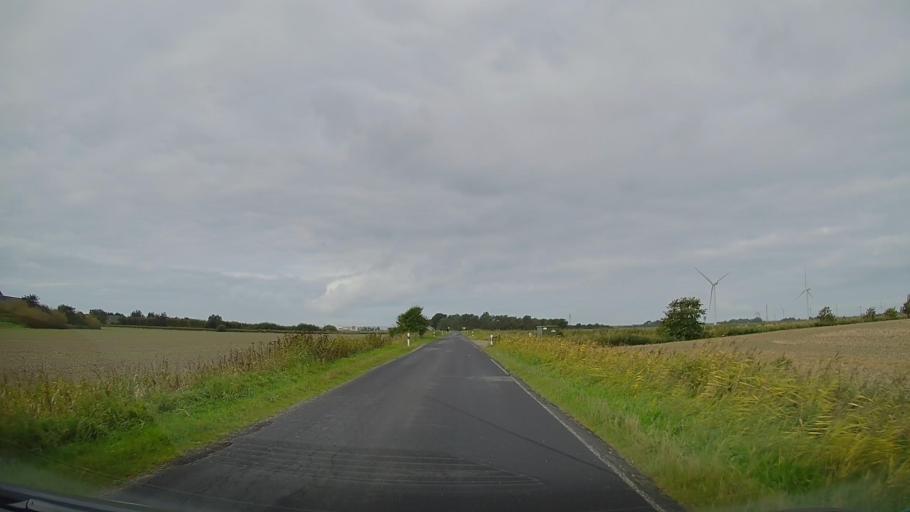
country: DE
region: Schleswig-Holstein
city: Emmelsbull-Horsbull
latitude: 54.8064
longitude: 8.6721
